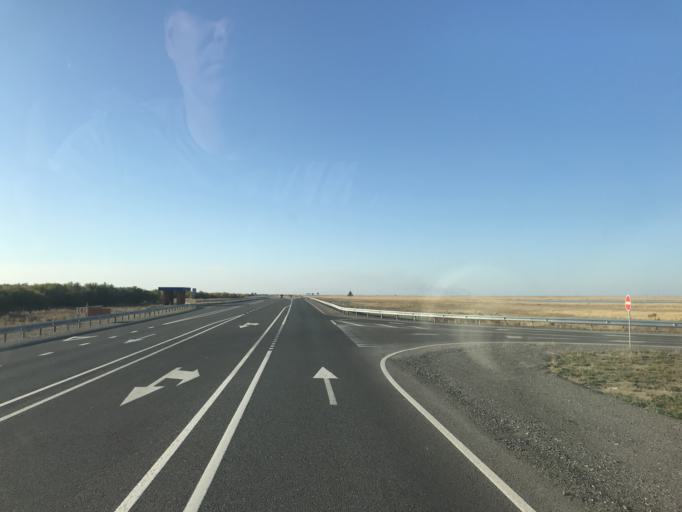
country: KZ
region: Pavlodar
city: Aksu
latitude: 52.0152
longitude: 77.2371
